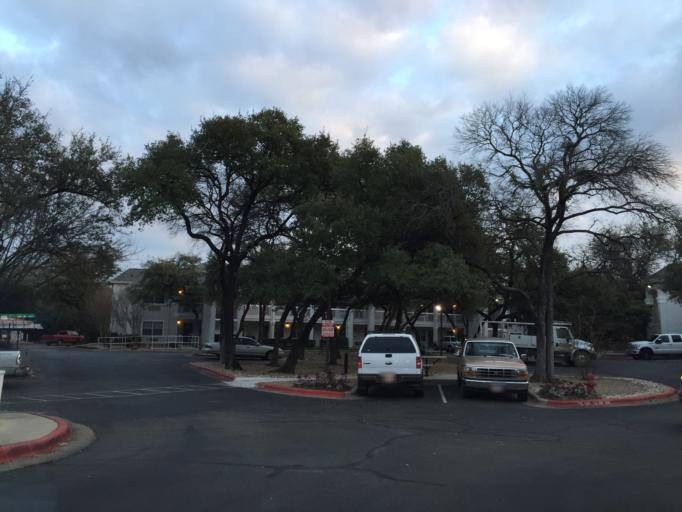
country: US
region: Texas
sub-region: Williamson County
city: Jollyville
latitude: 30.4250
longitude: -97.7549
